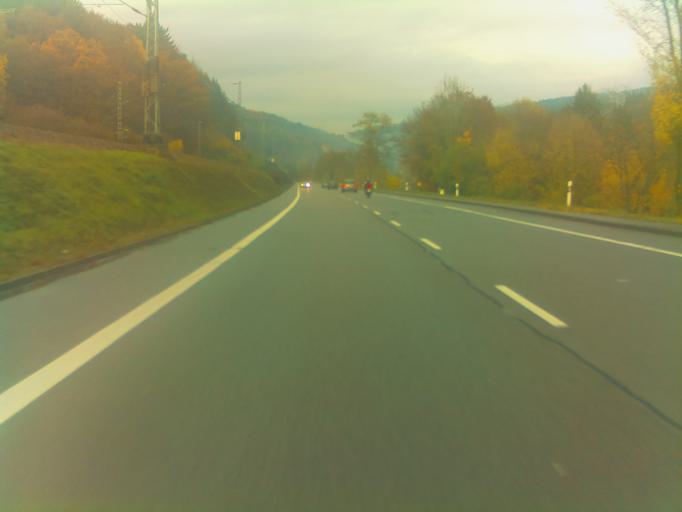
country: DE
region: Hesse
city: Neckarsteinach
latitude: 49.4029
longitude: 8.8609
